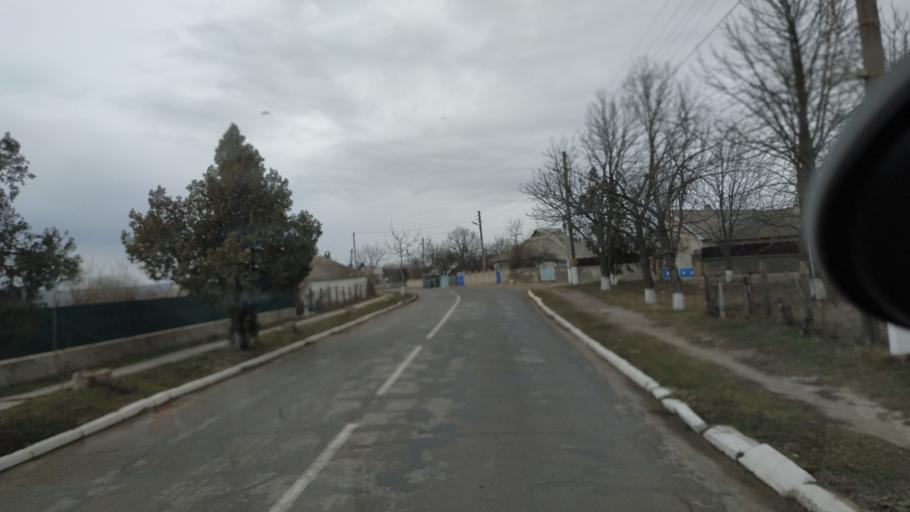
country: MD
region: Telenesti
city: Cocieri
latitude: 47.3037
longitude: 29.1130
